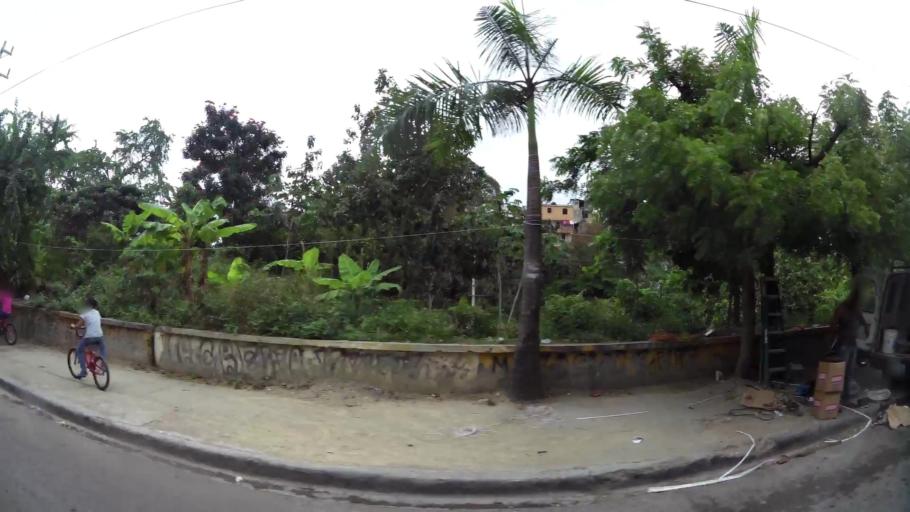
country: DO
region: Nacional
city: La Agustina
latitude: 18.4994
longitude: -69.9316
